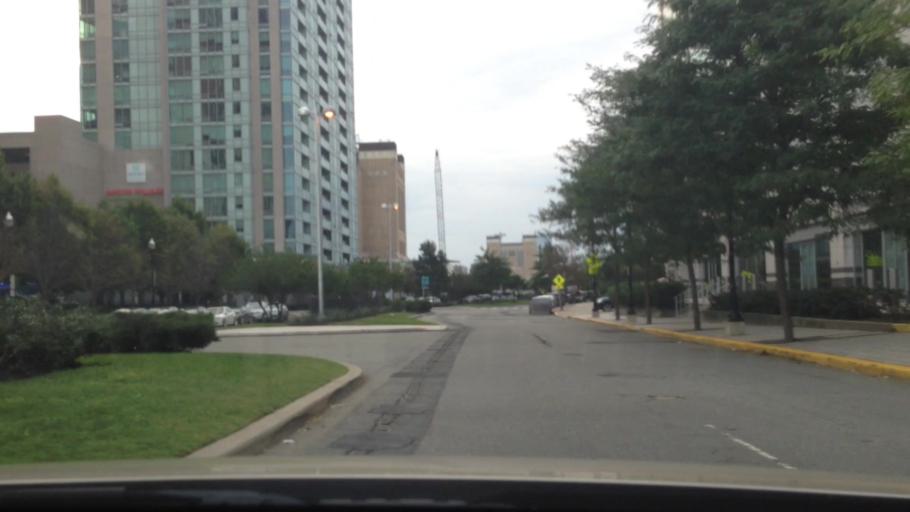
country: US
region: New Jersey
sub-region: Hudson County
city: Hoboken
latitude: 40.7292
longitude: -74.0344
